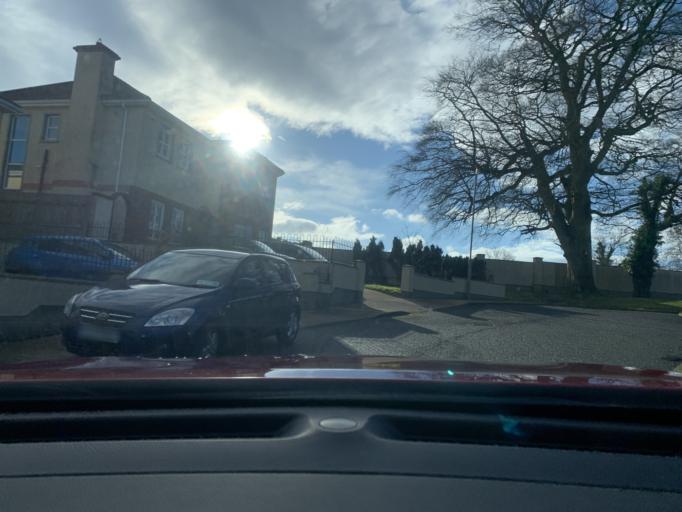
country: IE
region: Connaught
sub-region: Sligo
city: Sligo
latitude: 54.2699
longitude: -8.5060
